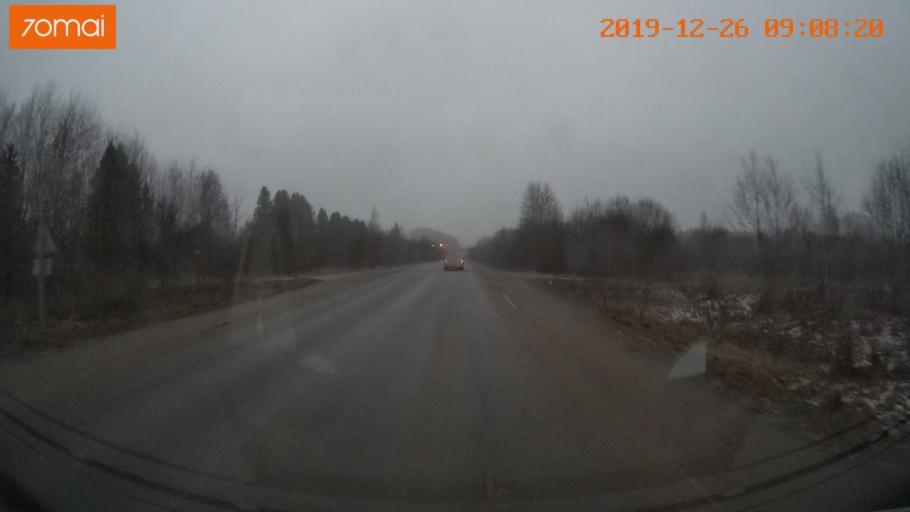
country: RU
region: Vologda
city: Gryazovets
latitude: 58.8556
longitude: 40.2481
